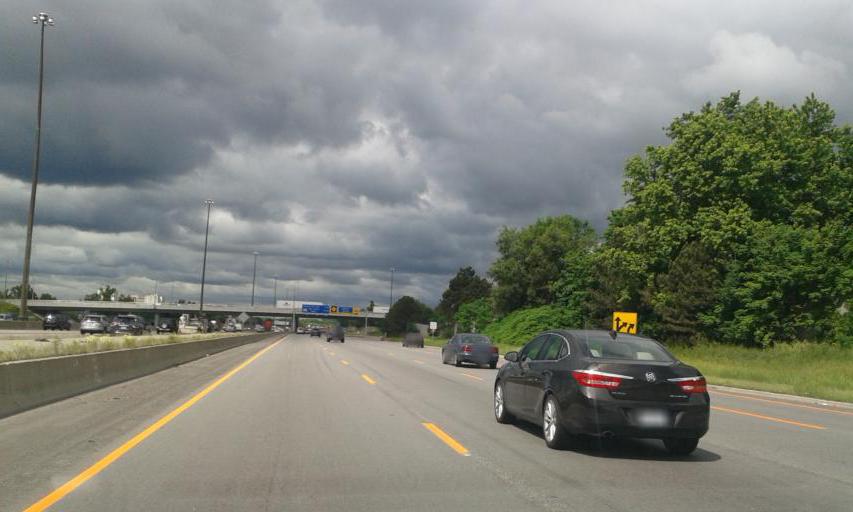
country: CA
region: Ontario
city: Scarborough
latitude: 43.7717
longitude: -79.3002
